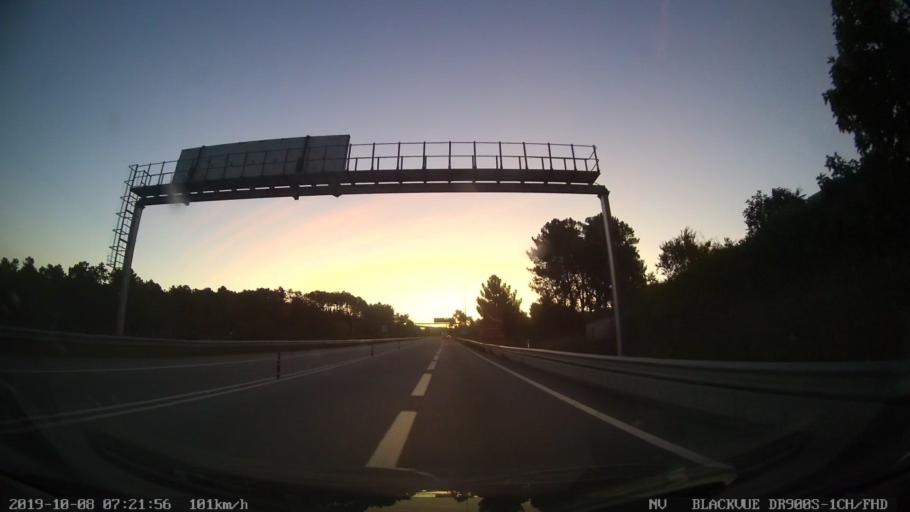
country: PT
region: Vila Real
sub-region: Vila Real
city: Vila Real
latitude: 41.3164
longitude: -7.7213
